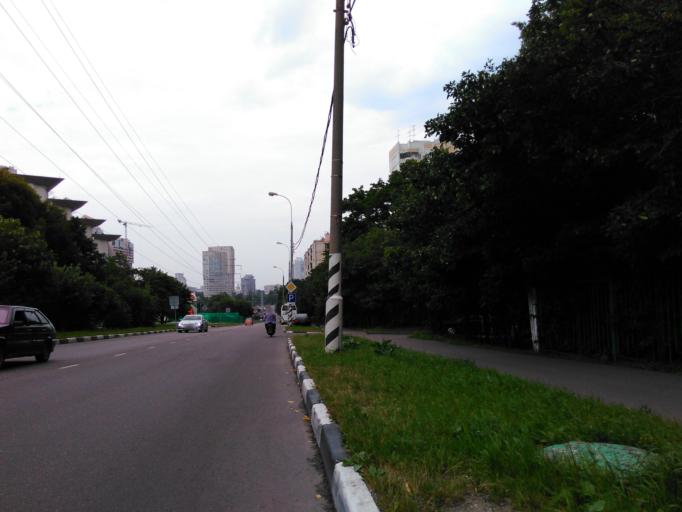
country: RU
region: Moskovskaya
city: Semenovskoye
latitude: 55.6761
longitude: 37.5492
